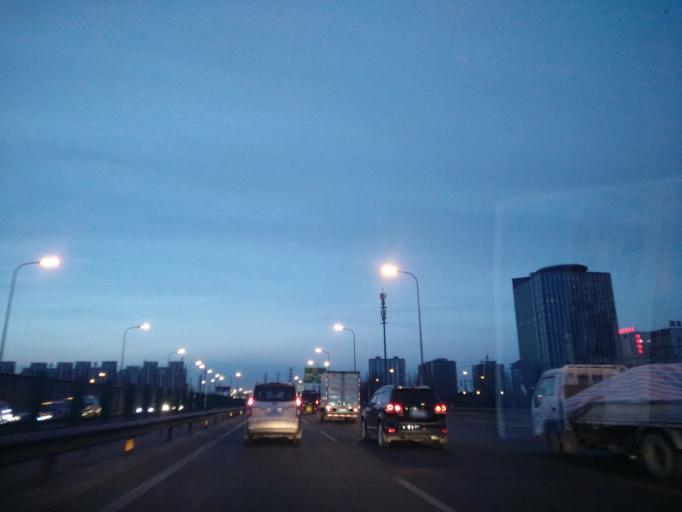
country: CN
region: Beijing
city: Dongfeng
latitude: 39.9138
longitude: 116.5378
